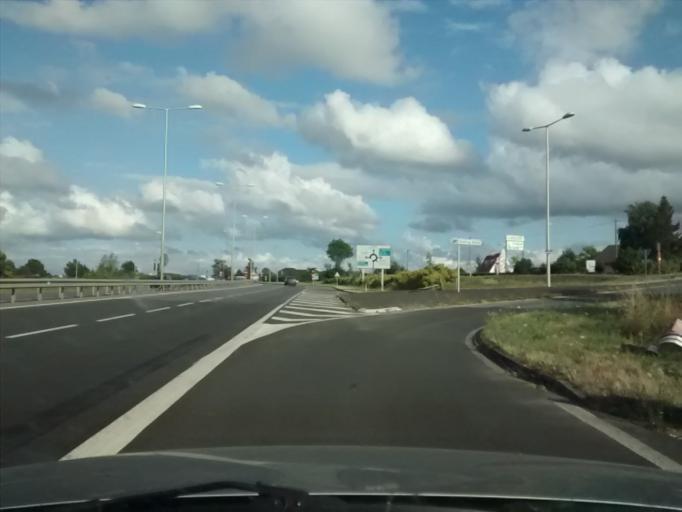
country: FR
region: Pays de la Loire
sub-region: Departement de la Mayenne
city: Change
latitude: 48.0816
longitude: -0.7984
